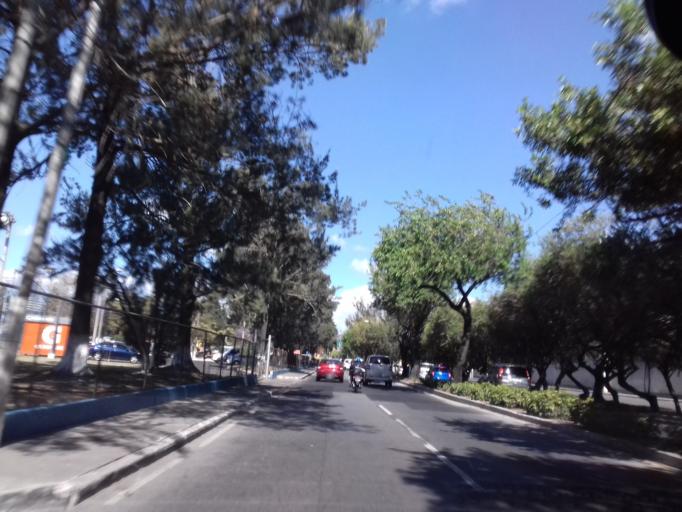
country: GT
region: Guatemala
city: Guatemala City
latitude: 14.6158
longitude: -90.5068
